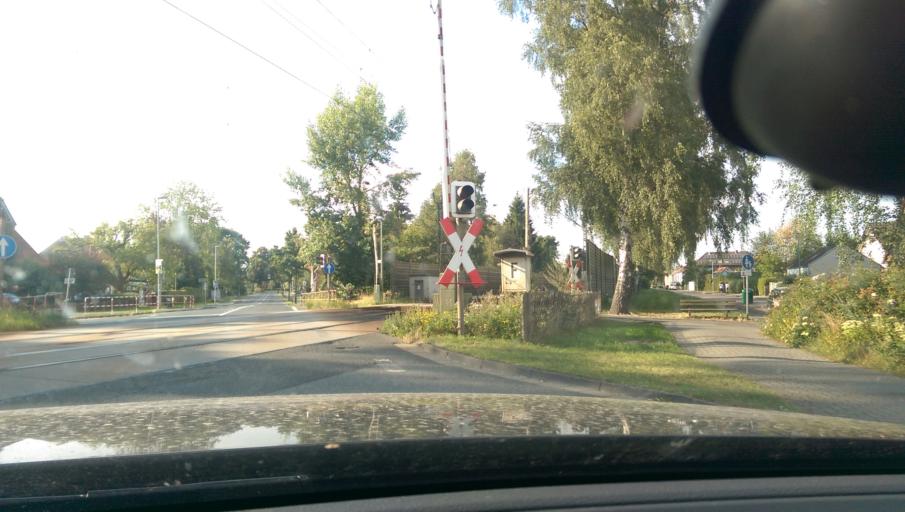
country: DE
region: Lower Saxony
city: Neustadt am Rubenberge
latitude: 52.5073
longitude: 9.4557
